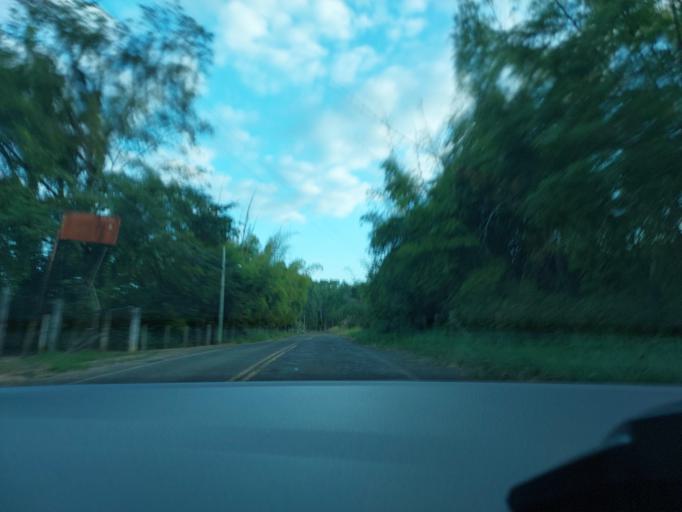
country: BR
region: Rio de Janeiro
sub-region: Natividade
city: Natividade
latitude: -21.1888
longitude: -42.1055
